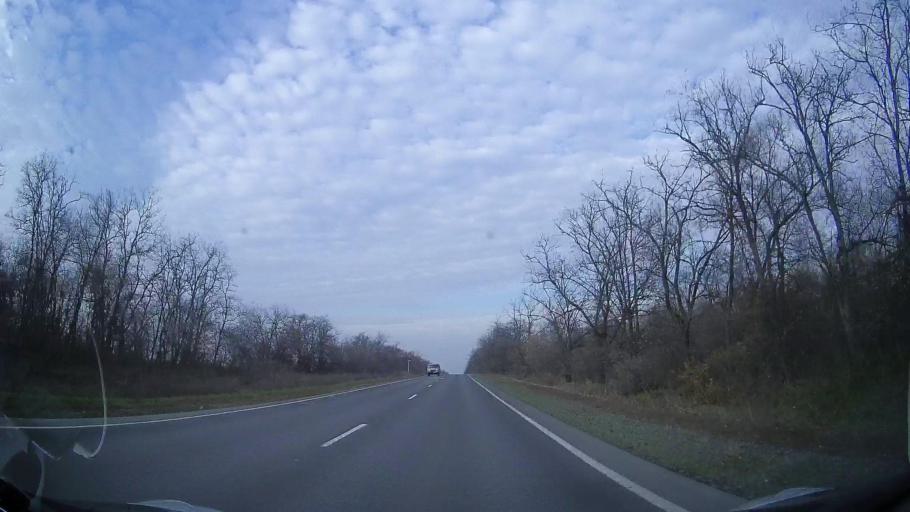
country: RU
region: Rostov
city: Bagayevskaya
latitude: 47.1218
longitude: 40.2767
